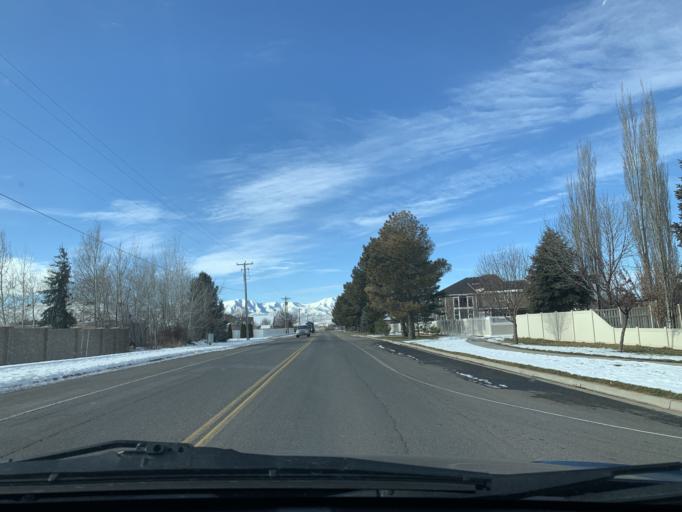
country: US
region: Utah
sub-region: Utah County
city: Lehi
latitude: 40.4208
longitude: -111.8254
